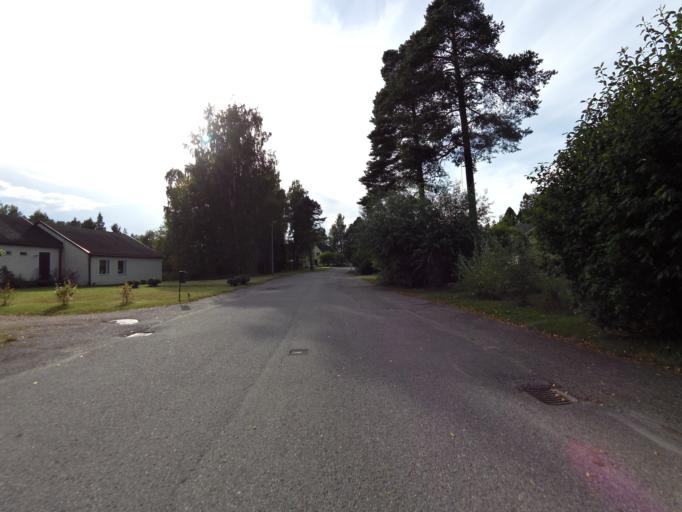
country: SE
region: Gaevleborg
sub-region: Gavle Kommun
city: Gavle
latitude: 60.6804
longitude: 17.2354
